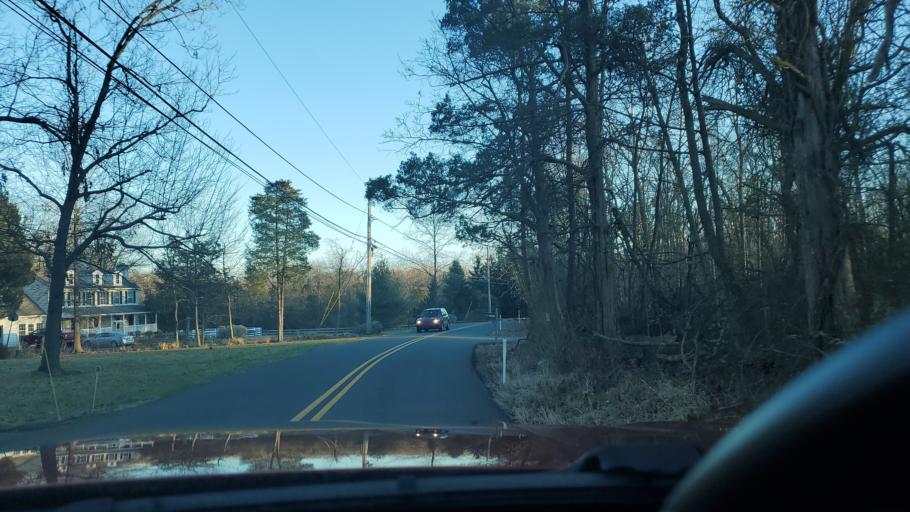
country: US
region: Pennsylvania
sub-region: Montgomery County
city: Woxall
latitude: 40.3095
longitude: -75.4891
